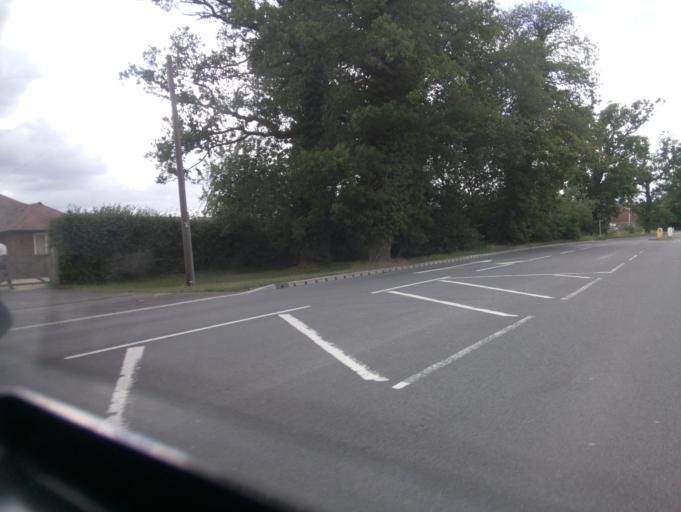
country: GB
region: England
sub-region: Warwickshire
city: Nuneaton
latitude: 52.5402
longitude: -1.4668
